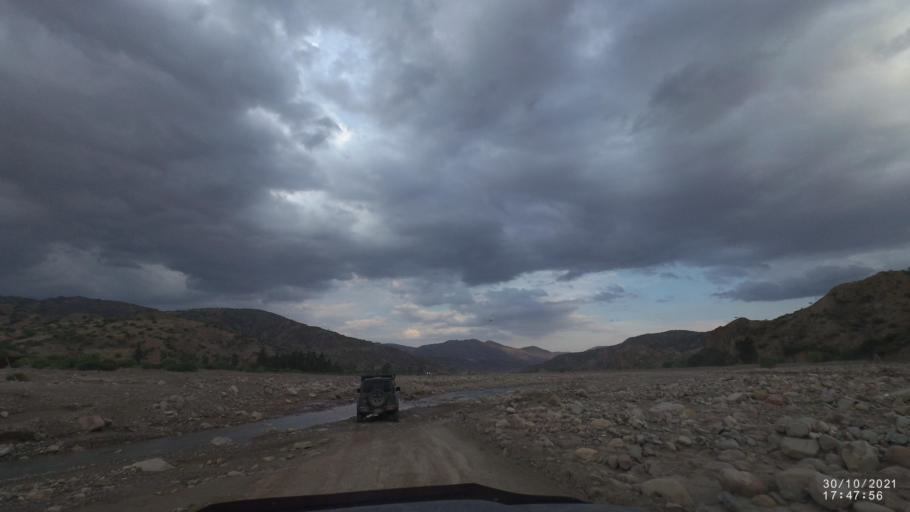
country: BO
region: Cochabamba
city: Sipe Sipe
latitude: -17.5347
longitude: -66.5211
